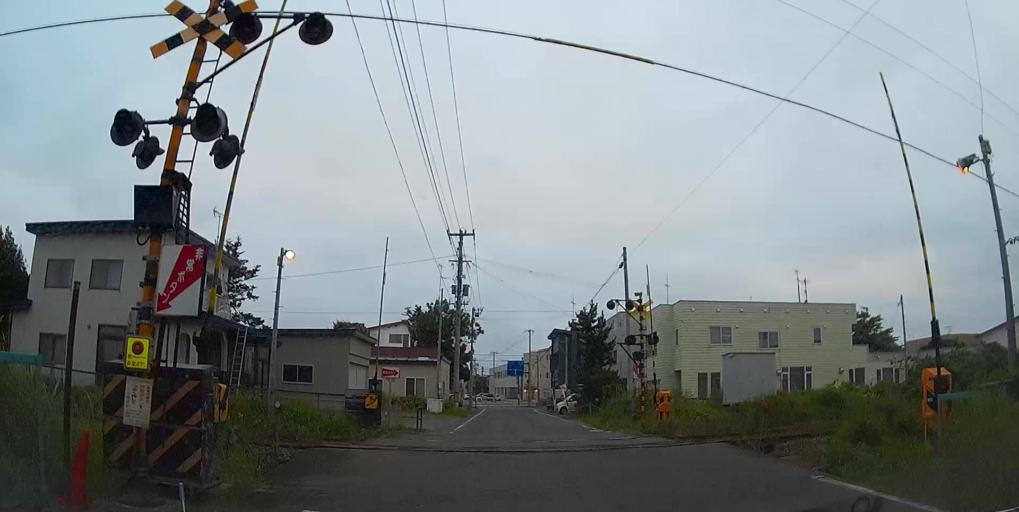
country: JP
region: Hokkaido
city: Nanae
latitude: 42.2566
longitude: 140.2672
